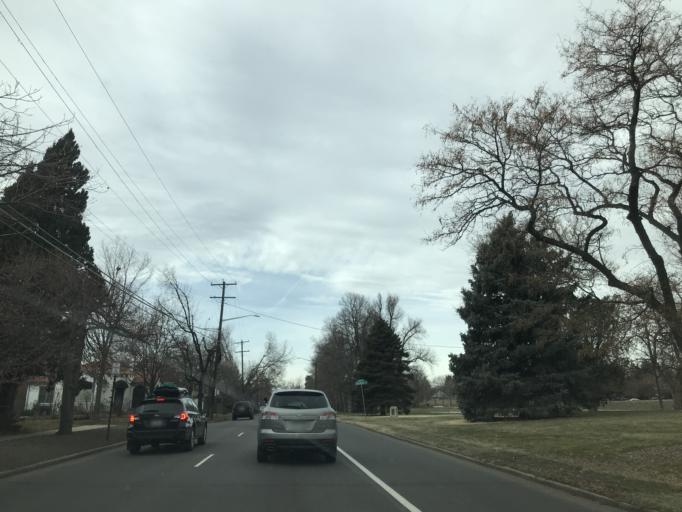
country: US
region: Colorado
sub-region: Denver County
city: Denver
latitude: 39.7292
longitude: -104.9562
